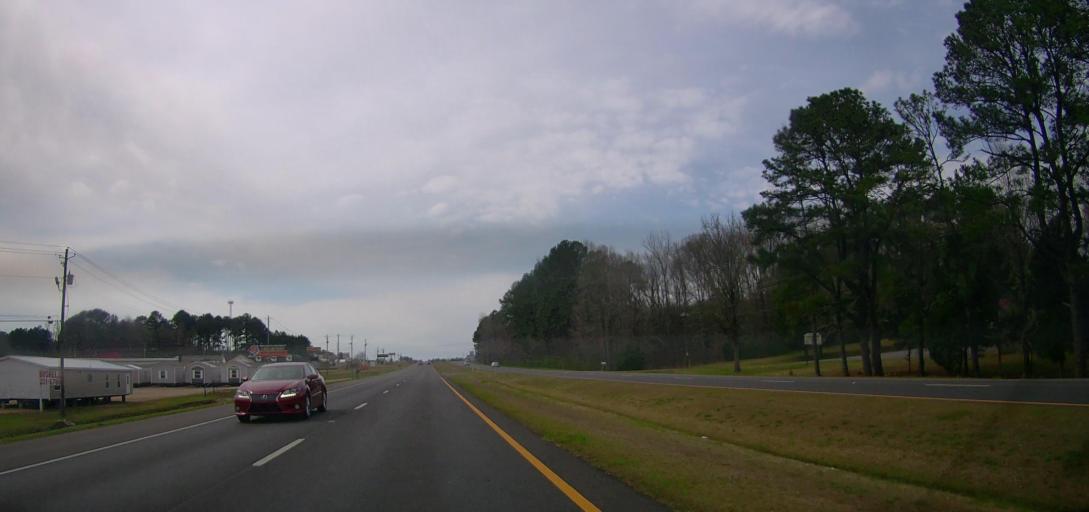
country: US
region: Alabama
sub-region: Walker County
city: Jasper
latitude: 33.8344
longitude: -87.2198
